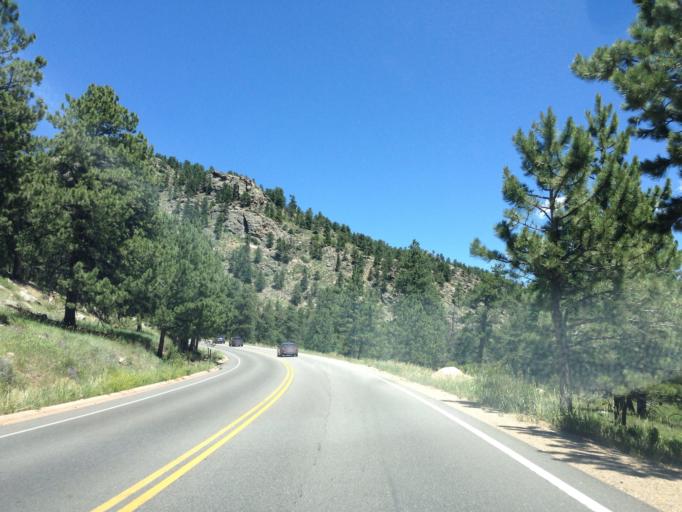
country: US
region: Colorado
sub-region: Larimer County
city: Estes Park
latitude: 40.3479
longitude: -105.5776
